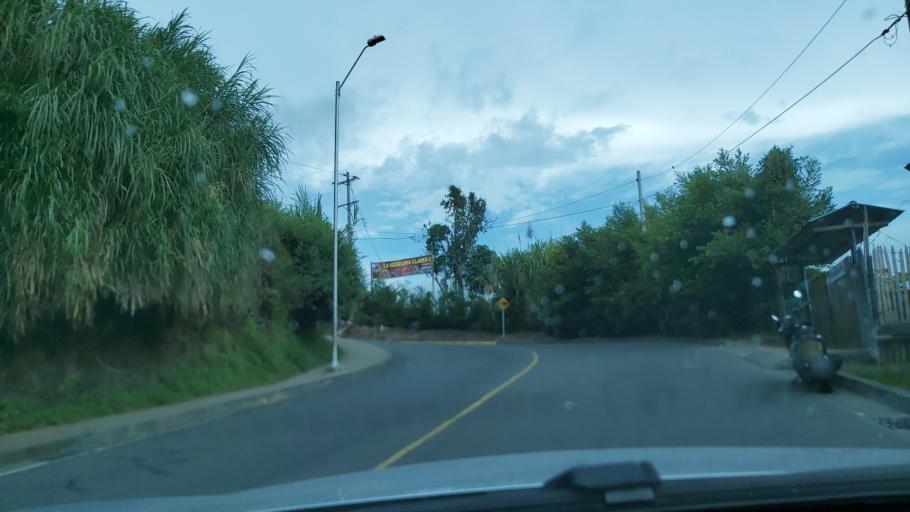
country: CO
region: Risaralda
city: Pereira
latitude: 4.7953
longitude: -75.7095
